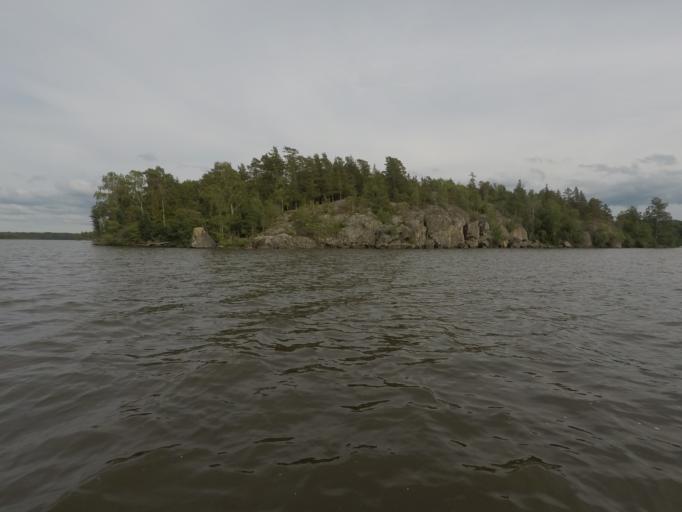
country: SE
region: Soedermanland
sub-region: Eskilstuna Kommun
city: Kvicksund
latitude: 59.4785
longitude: 16.3980
